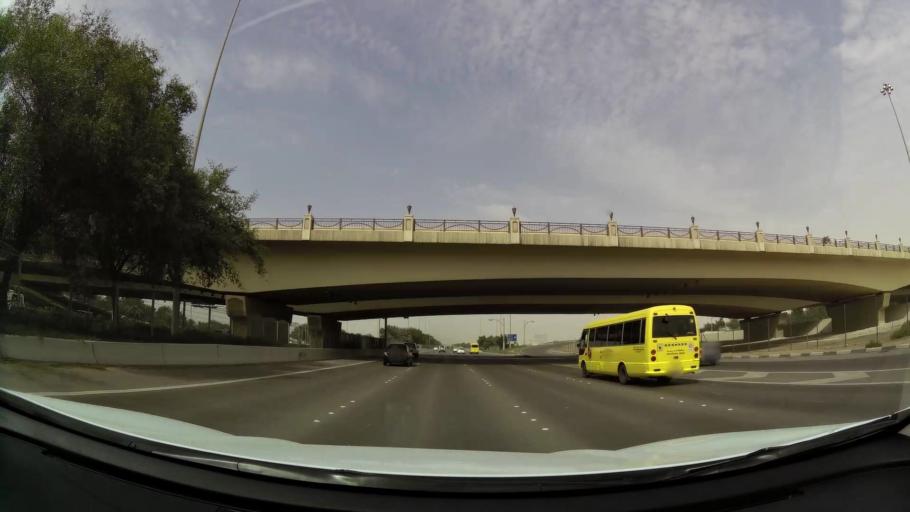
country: AE
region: Abu Dhabi
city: Abu Dhabi
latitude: 24.3467
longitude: 54.5263
